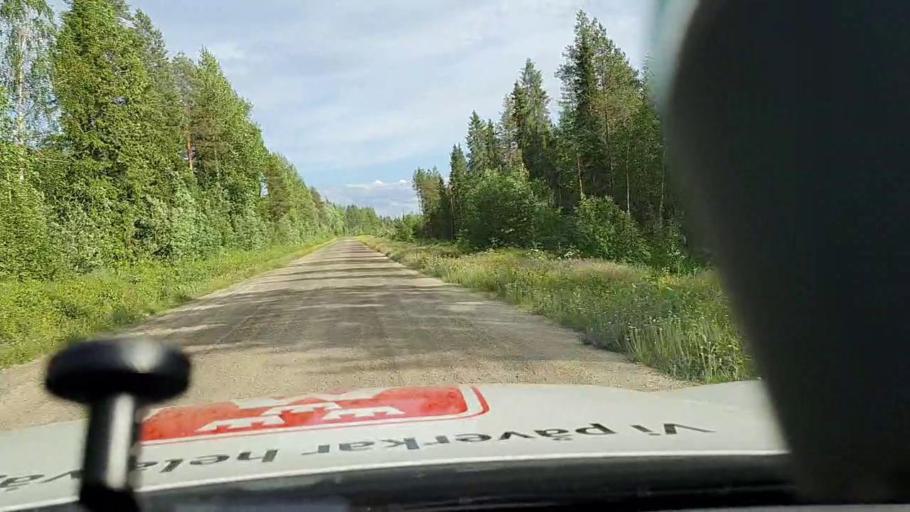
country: SE
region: Norrbotten
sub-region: Alvsbyns Kommun
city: AElvsbyn
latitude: 66.1786
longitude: 21.2338
